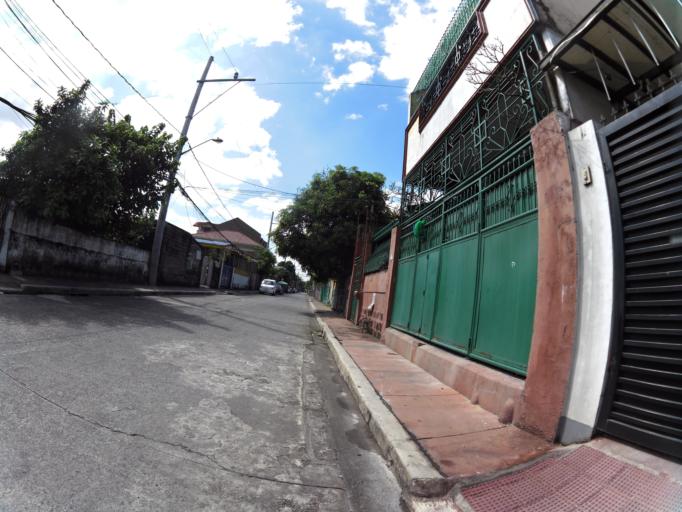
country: PH
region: Calabarzon
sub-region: Province of Rizal
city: Antipolo
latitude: 14.6412
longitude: 121.1129
